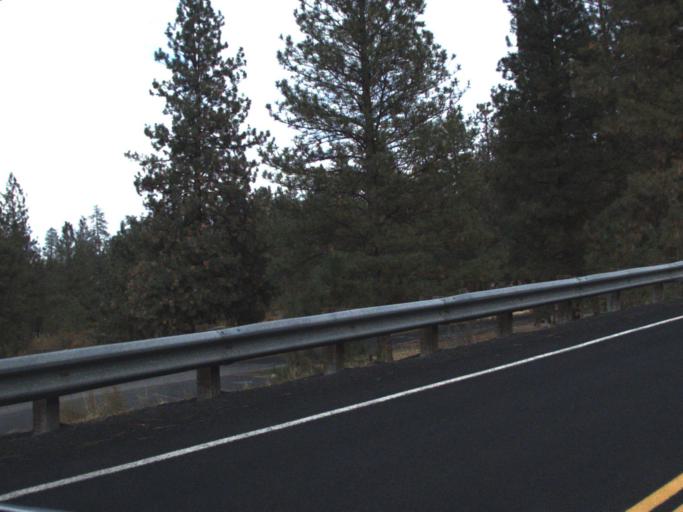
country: US
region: Washington
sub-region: Lincoln County
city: Davenport
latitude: 47.9084
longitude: -118.3101
